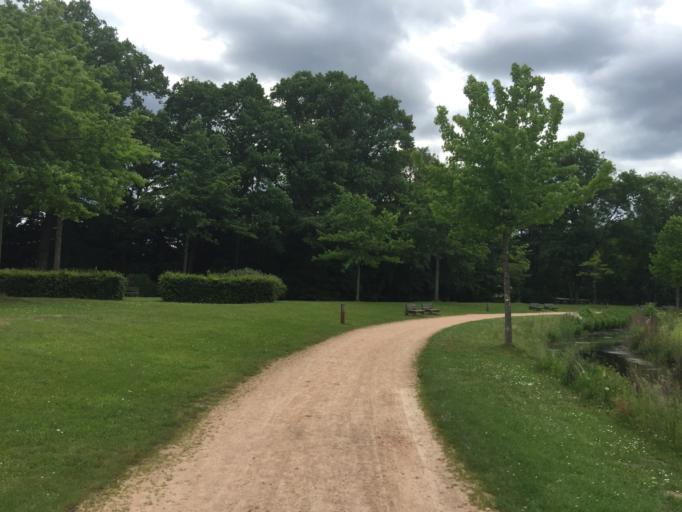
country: FR
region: Auvergne
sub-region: Departement du Puy-de-Dome
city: Ambert
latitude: 45.5471
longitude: 3.7337
